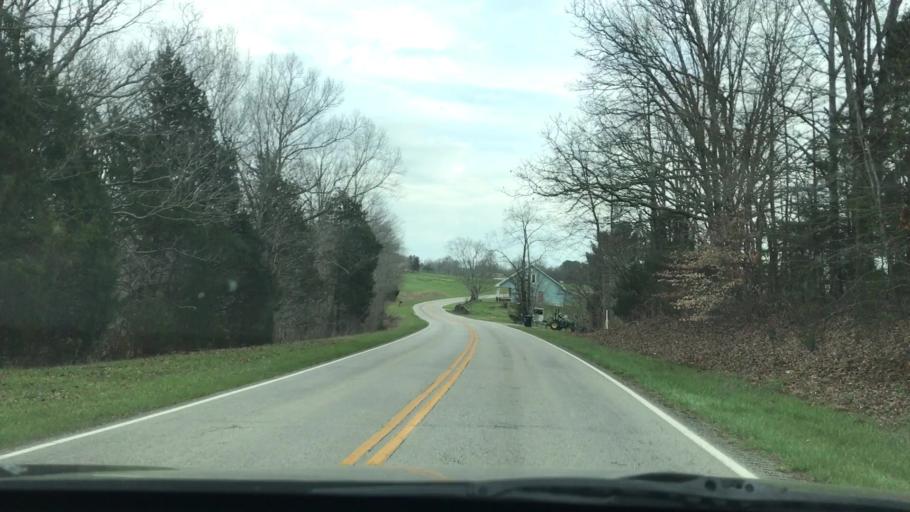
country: US
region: Kentucky
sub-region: Hart County
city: Munfordville
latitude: 37.3010
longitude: -85.7641
